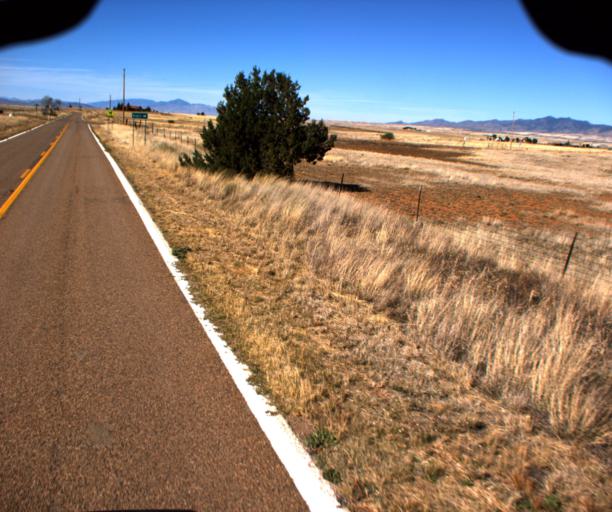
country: US
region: Arizona
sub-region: Cochise County
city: Huachuca City
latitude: 31.6578
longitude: -110.6049
